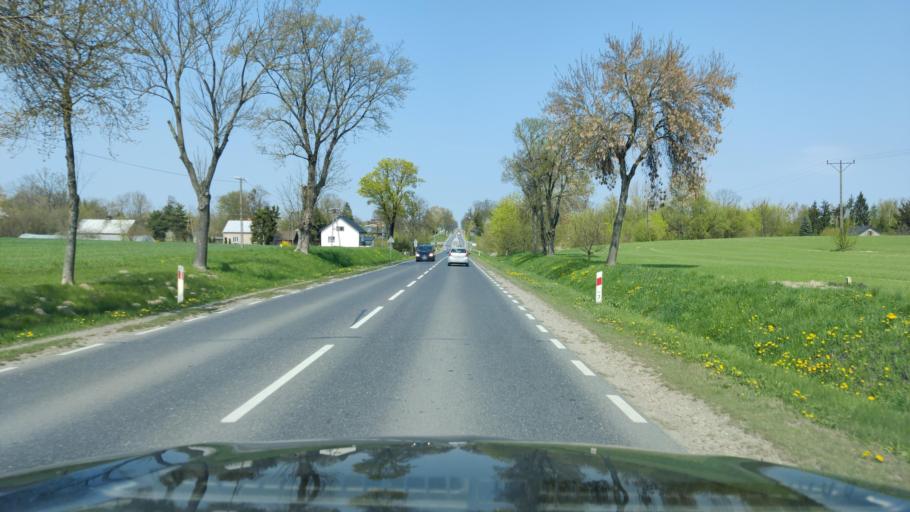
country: PL
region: Masovian Voivodeship
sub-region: Powiat pultuski
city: Pultusk
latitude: 52.6651
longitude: 21.0816
